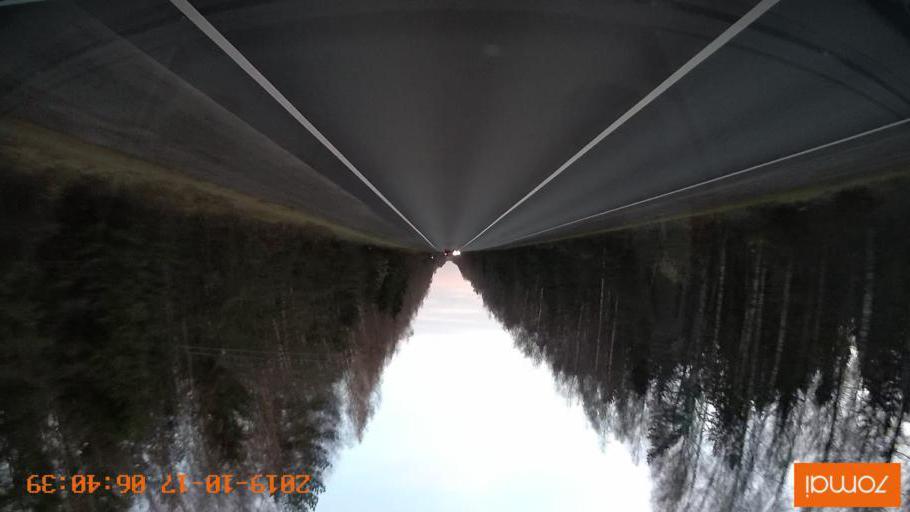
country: RU
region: Ivanovo
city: Nerl'
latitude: 56.6262
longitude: 40.5676
